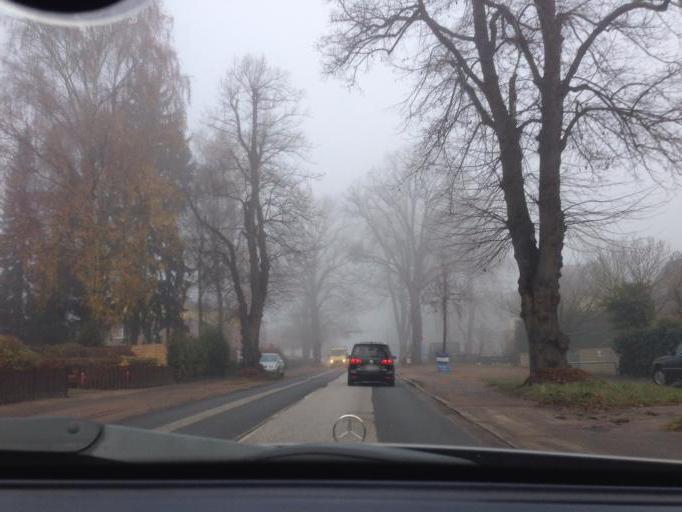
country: DE
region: Hamburg
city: Farmsen-Berne
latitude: 53.6201
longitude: 10.1628
